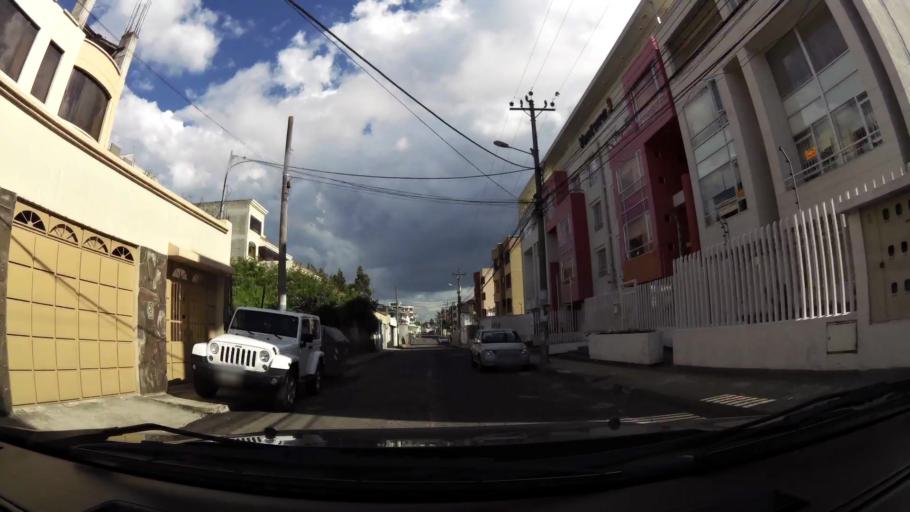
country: EC
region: Pichincha
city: Quito
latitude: -0.1079
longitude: -78.4834
